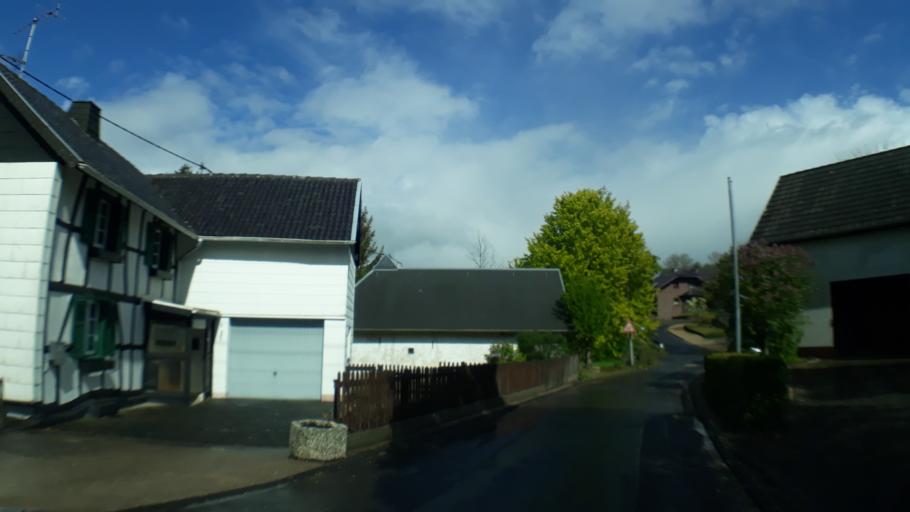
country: DE
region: North Rhine-Westphalia
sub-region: Regierungsbezirk Koln
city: Schleiden
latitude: 50.4907
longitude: 6.5177
